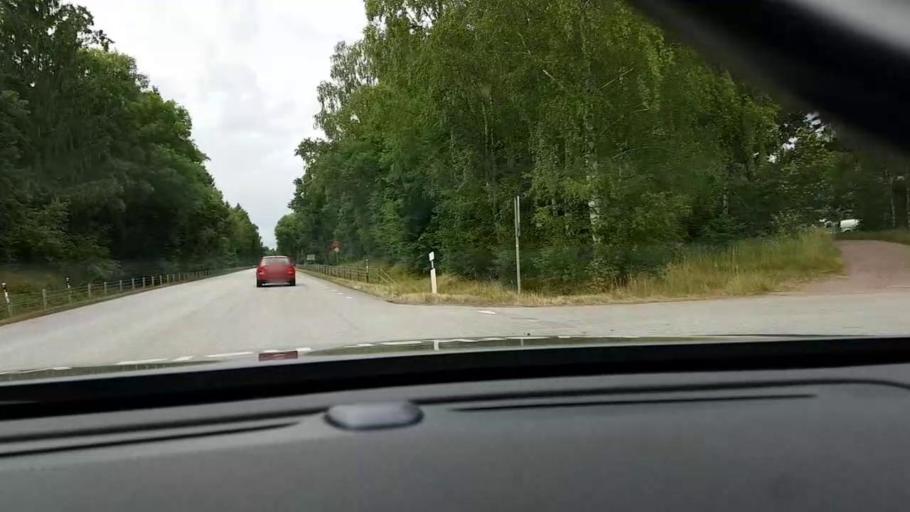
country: SE
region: Skane
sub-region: Hoors Kommun
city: Satofta
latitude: 55.9107
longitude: 13.6019
